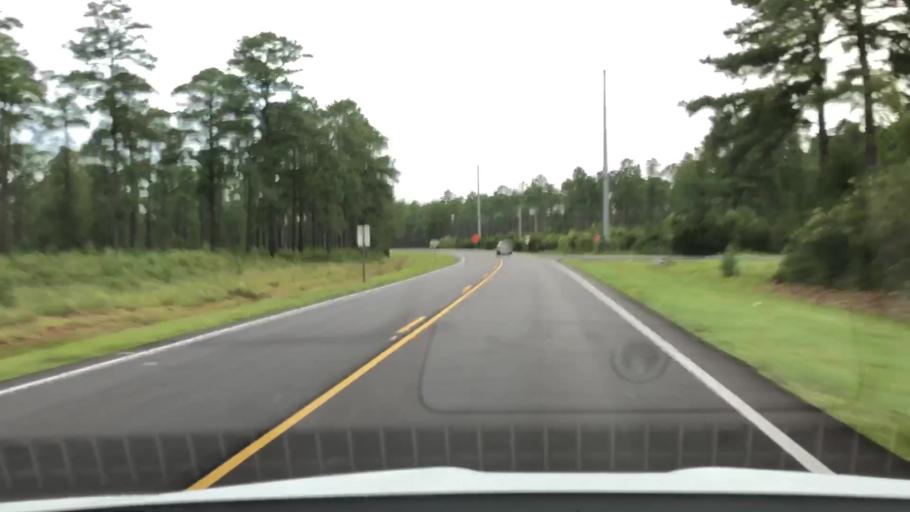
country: US
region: North Carolina
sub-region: Onslow County
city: Swansboro
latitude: 34.8073
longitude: -77.1341
